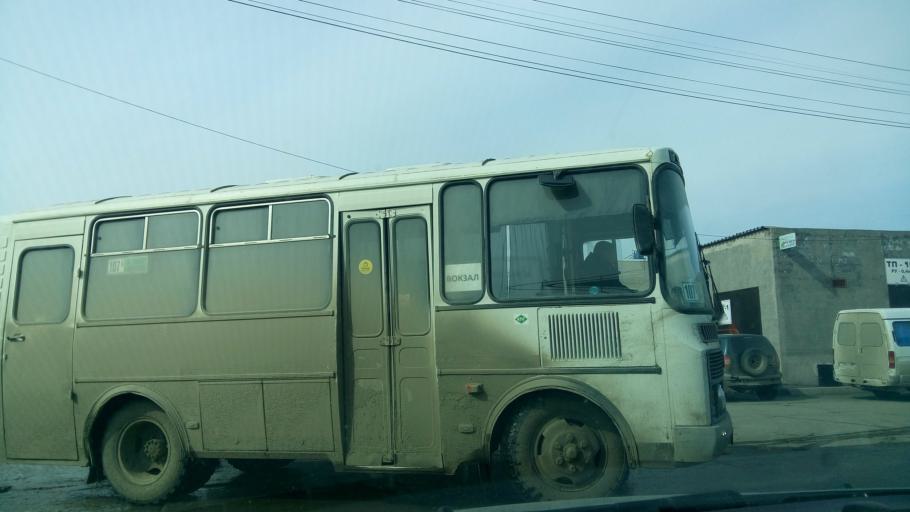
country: RU
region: Sverdlovsk
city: Nizhniy Tagil
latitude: 57.9078
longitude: 60.0235
